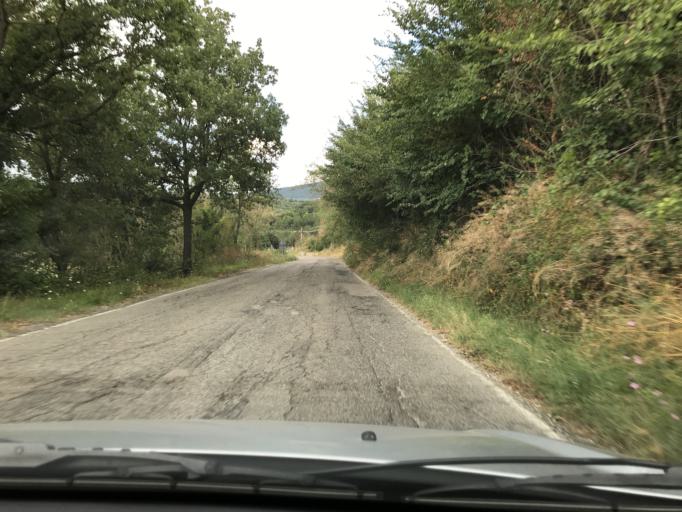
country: IT
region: Umbria
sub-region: Provincia di Terni
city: Montecchio
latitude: 42.6511
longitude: 12.2793
